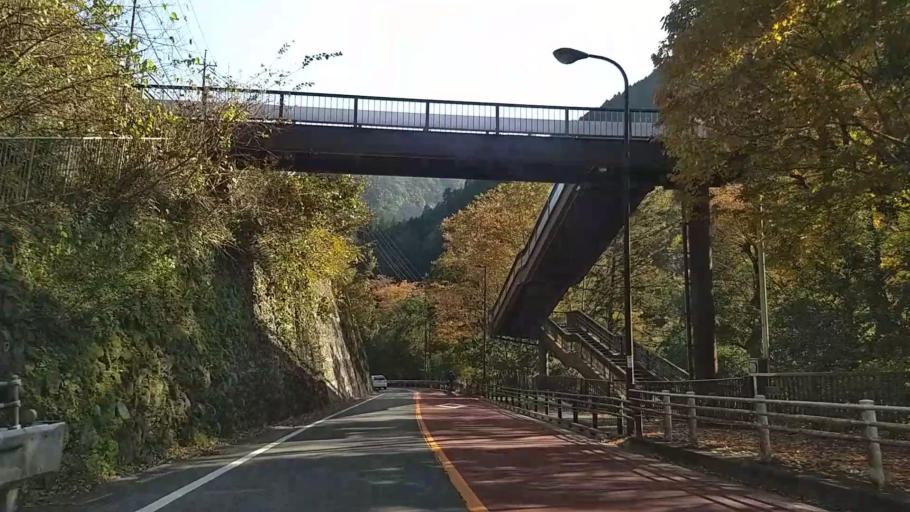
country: JP
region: Tokyo
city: Itsukaichi
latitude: 35.8030
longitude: 139.1041
